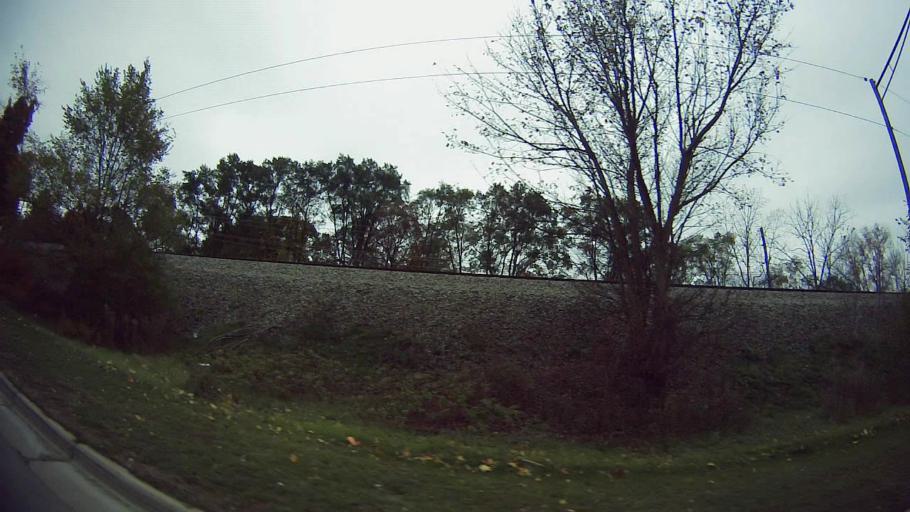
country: US
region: Michigan
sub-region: Oakland County
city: Waterford
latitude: 42.6765
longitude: -83.3591
